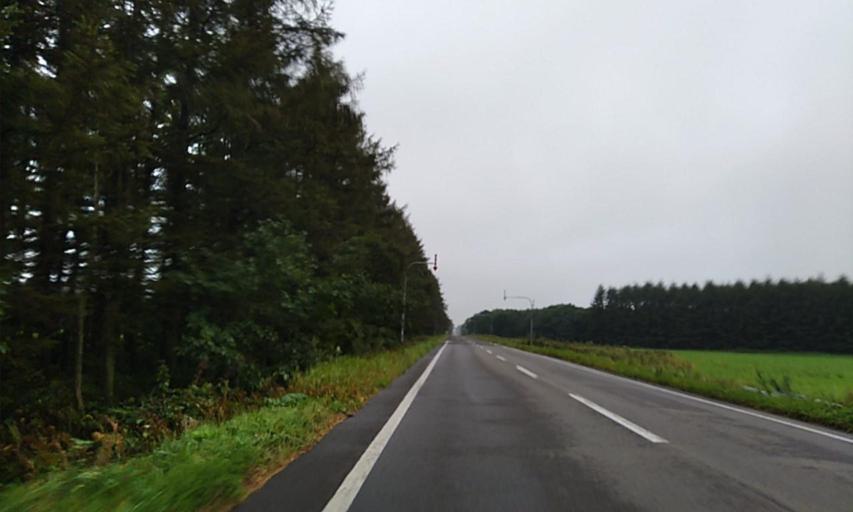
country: JP
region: Hokkaido
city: Shibetsu
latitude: 43.5220
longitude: 144.6874
